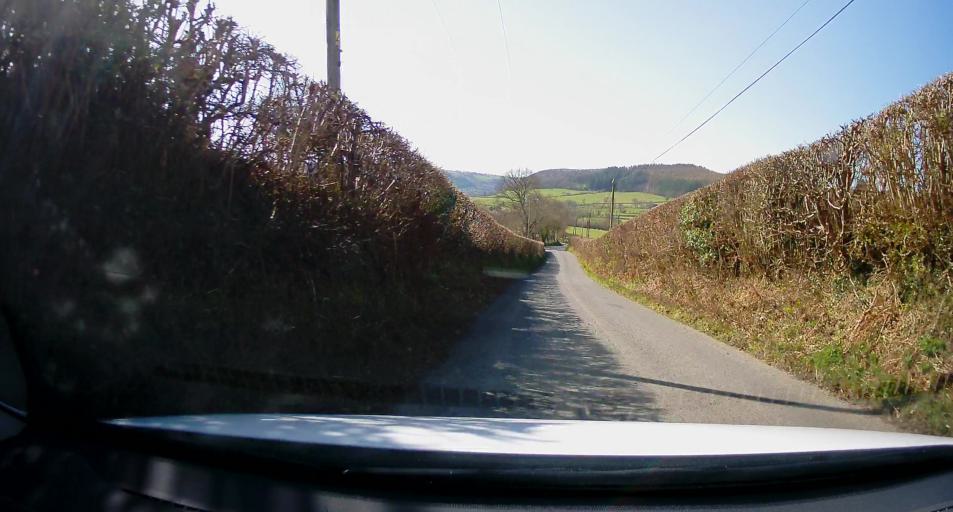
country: GB
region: Wales
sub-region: County of Ceredigion
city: Lledrod
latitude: 52.3534
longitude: -3.9358
